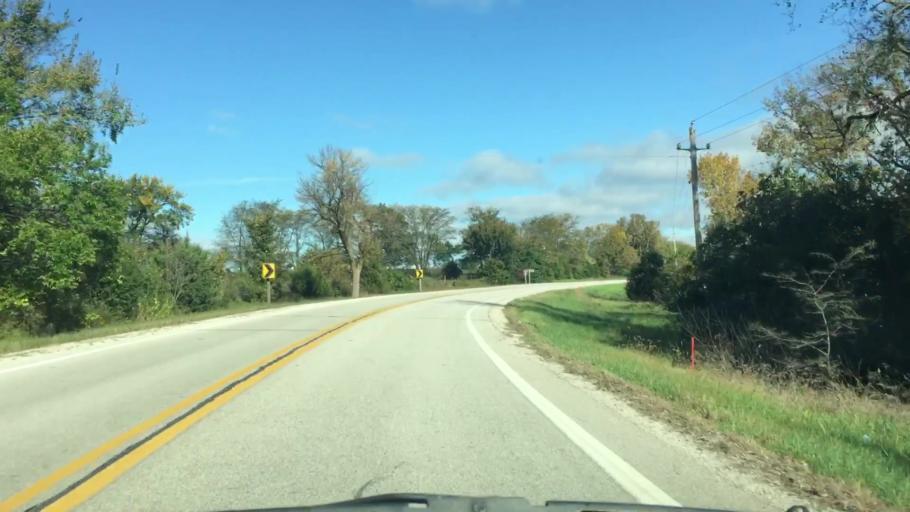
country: US
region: Iowa
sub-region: Decatur County
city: Leon
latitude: 40.7253
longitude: -93.7614
